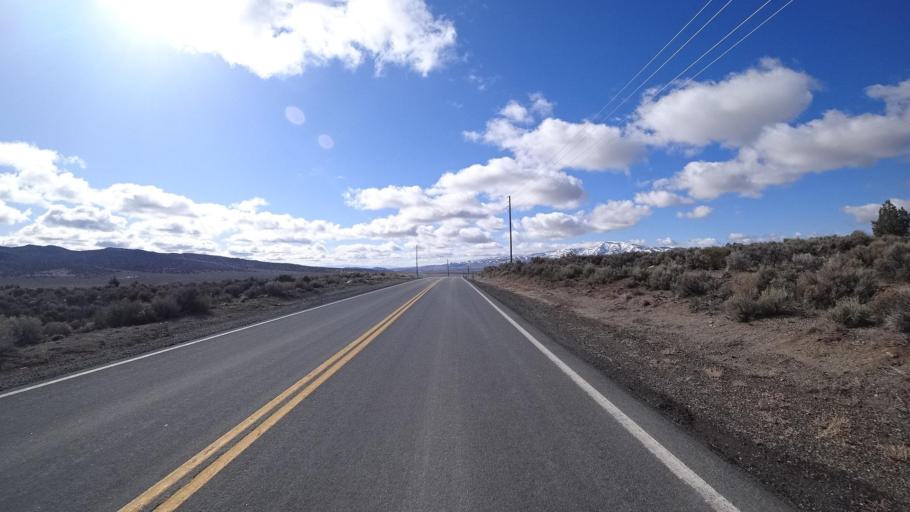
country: US
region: Nevada
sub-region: Washoe County
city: Lemmon Valley
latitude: 39.7261
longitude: -119.8810
